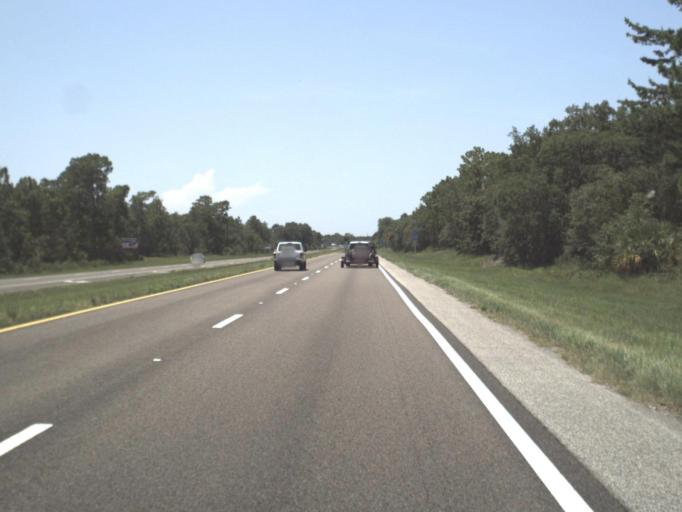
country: US
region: Florida
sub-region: Citrus County
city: Sugarmill Woods
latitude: 28.7168
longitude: -82.5419
